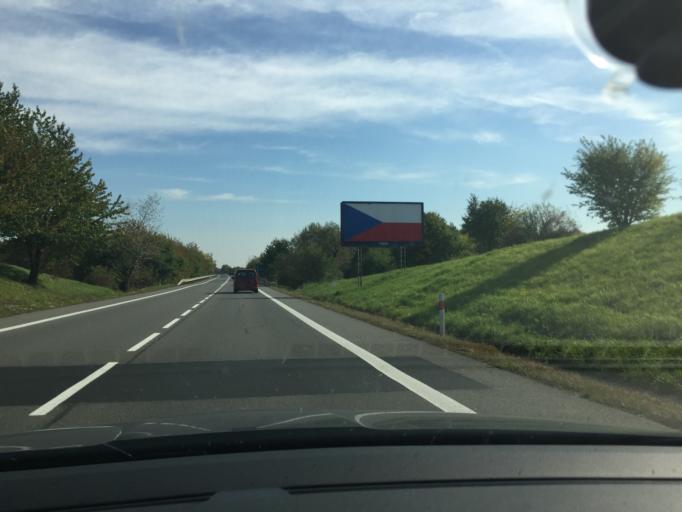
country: CZ
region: Central Bohemia
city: Planany
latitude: 50.0449
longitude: 15.0181
